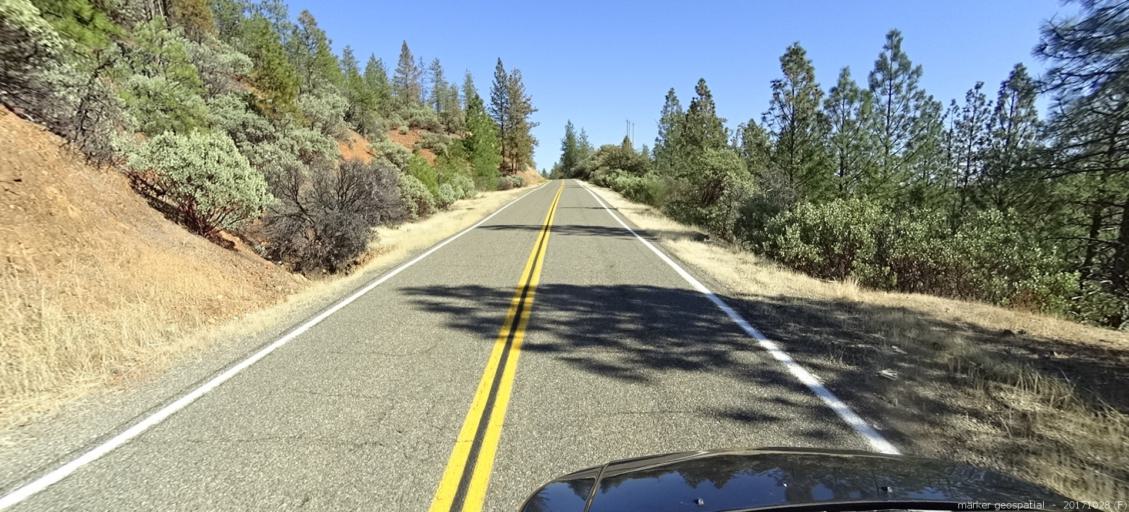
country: US
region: California
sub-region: Shasta County
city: Shasta
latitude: 40.6311
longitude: -122.4645
